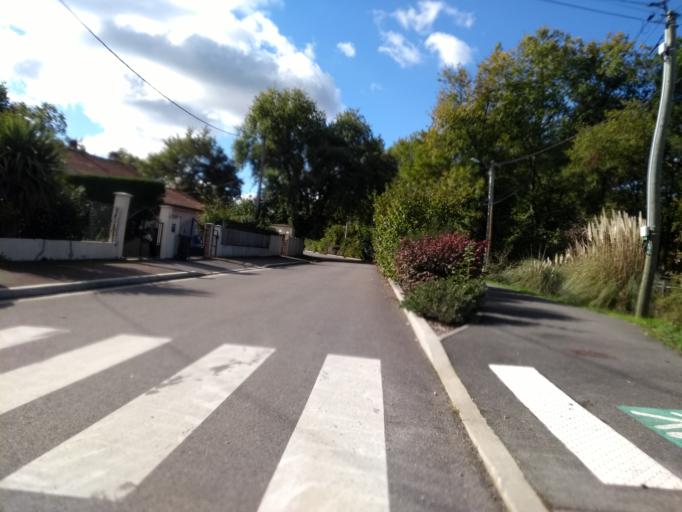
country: FR
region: Aquitaine
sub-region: Departement de la Gironde
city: Pessac
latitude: 44.8196
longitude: -0.6764
